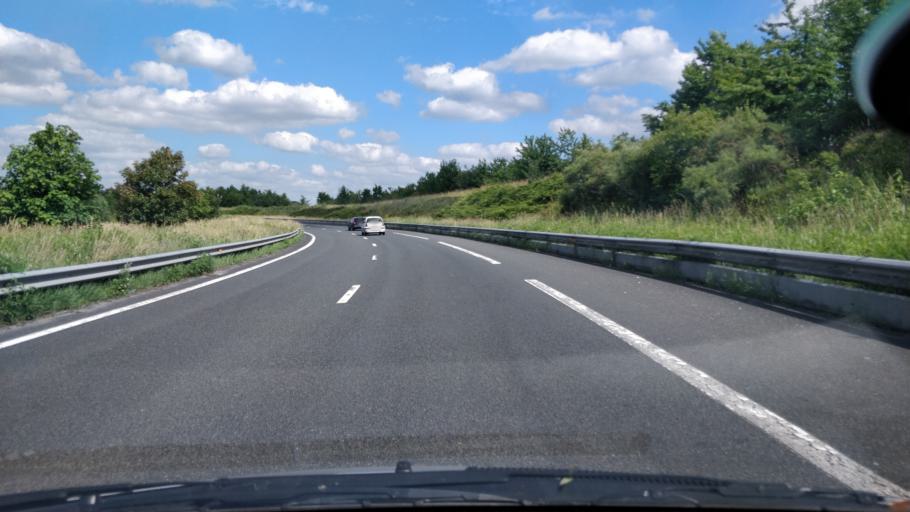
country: FR
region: Ile-de-France
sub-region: Departement de Seine-et-Marne
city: Serris
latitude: 48.8303
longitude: 2.7709
